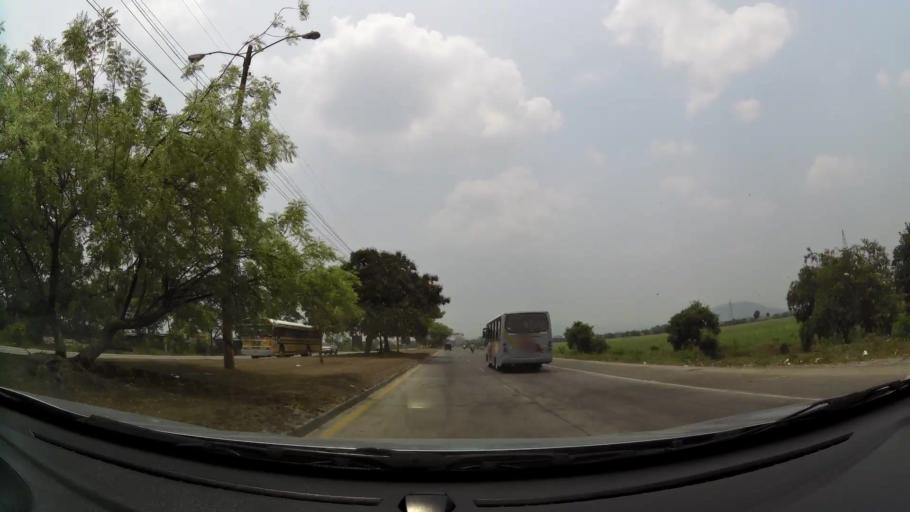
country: HN
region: Cortes
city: La Lima
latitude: 15.4505
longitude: -87.9456
